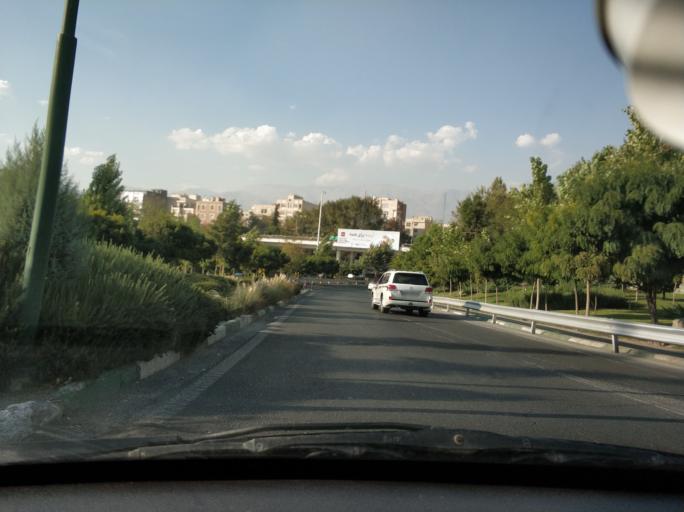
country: IR
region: Tehran
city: Tehran
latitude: 35.7422
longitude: 51.4624
